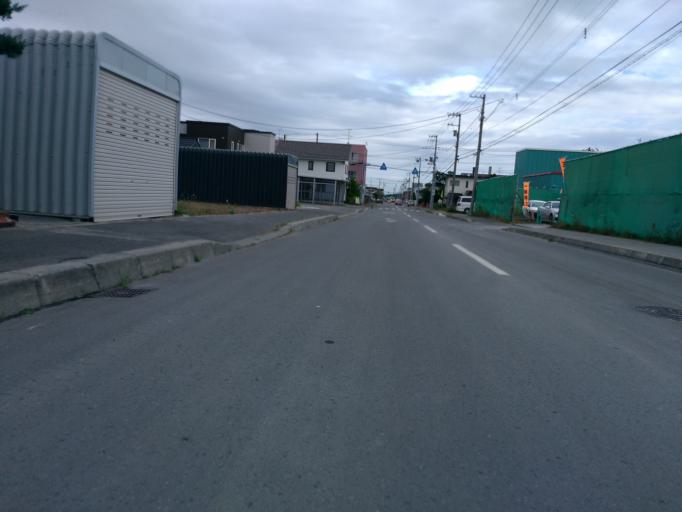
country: JP
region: Hokkaido
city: Ebetsu
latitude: 43.0829
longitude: 141.5280
